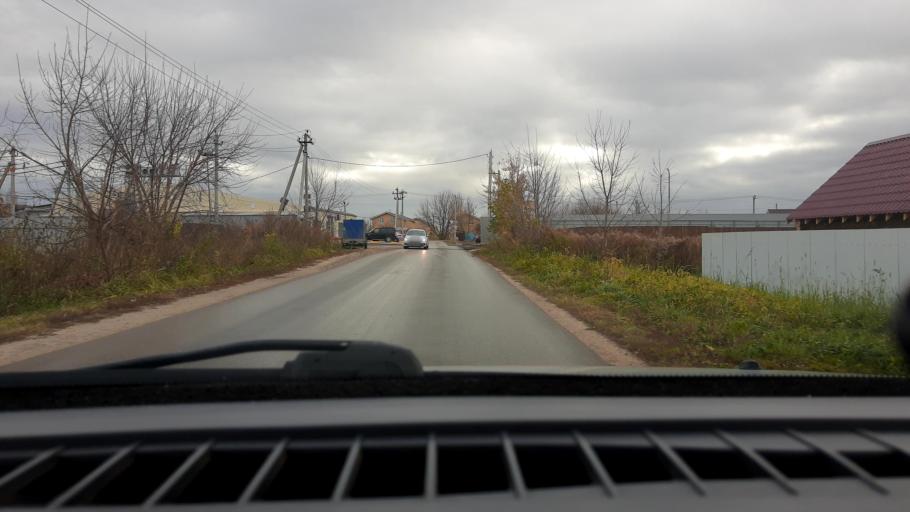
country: RU
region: Nizjnij Novgorod
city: Afonino
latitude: 56.2027
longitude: 44.1323
